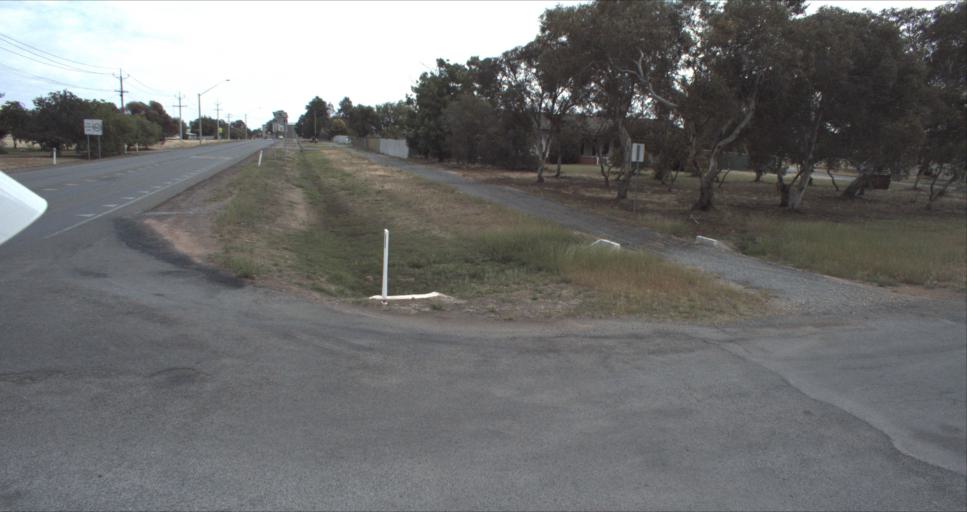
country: AU
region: New South Wales
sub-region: Leeton
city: Leeton
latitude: -34.5638
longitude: 146.3930
